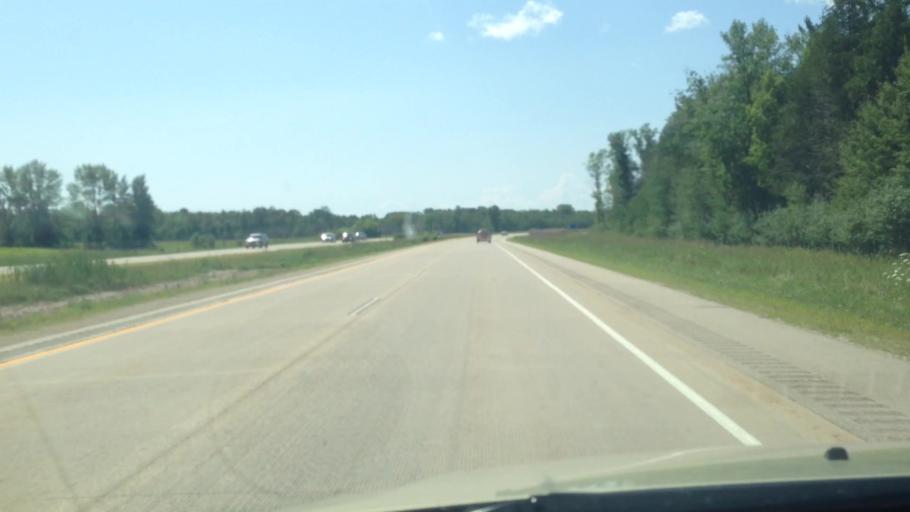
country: US
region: Wisconsin
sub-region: Oconto County
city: Oconto
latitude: 44.9306
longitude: -87.8703
